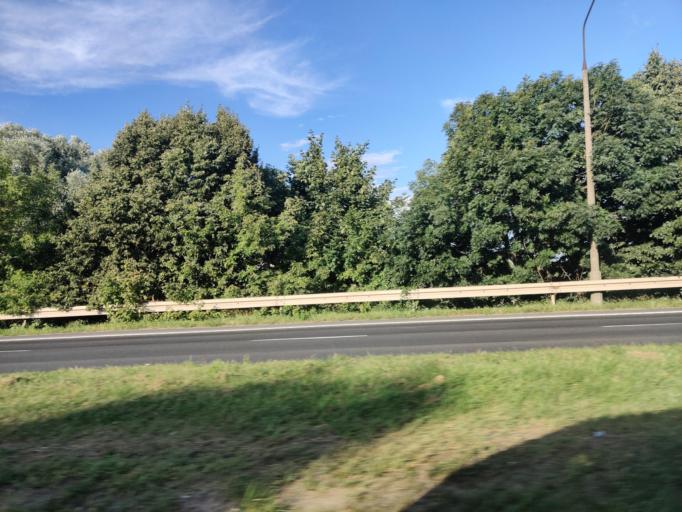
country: PL
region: Greater Poland Voivodeship
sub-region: Konin
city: Konin
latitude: 52.2162
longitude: 18.2551
